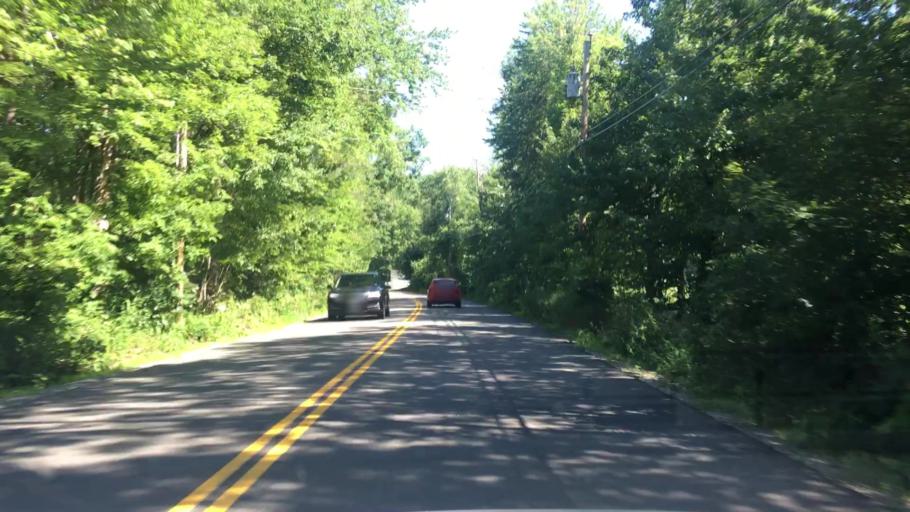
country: US
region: New Hampshire
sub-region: Rockingham County
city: Auburn
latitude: 43.0276
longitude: -71.3812
